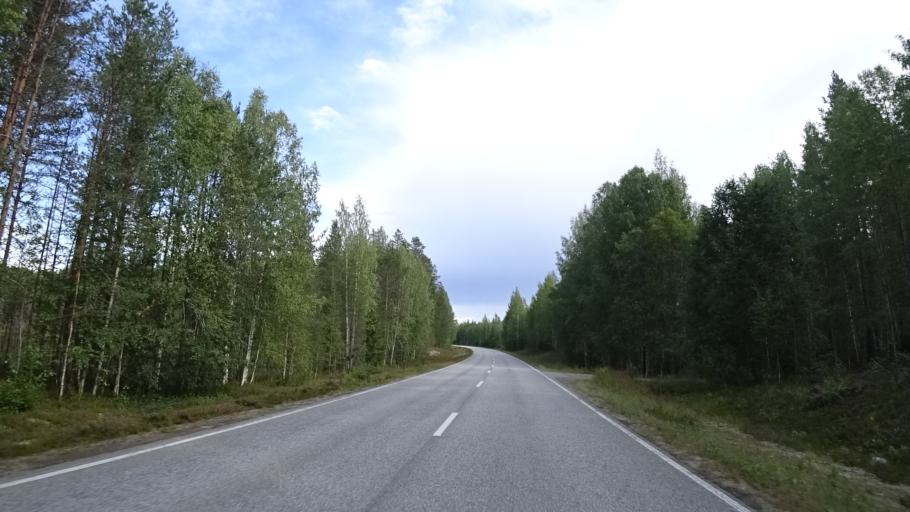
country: FI
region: North Karelia
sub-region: Joensuu
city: Ilomantsi
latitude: 62.6244
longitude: 31.1146
